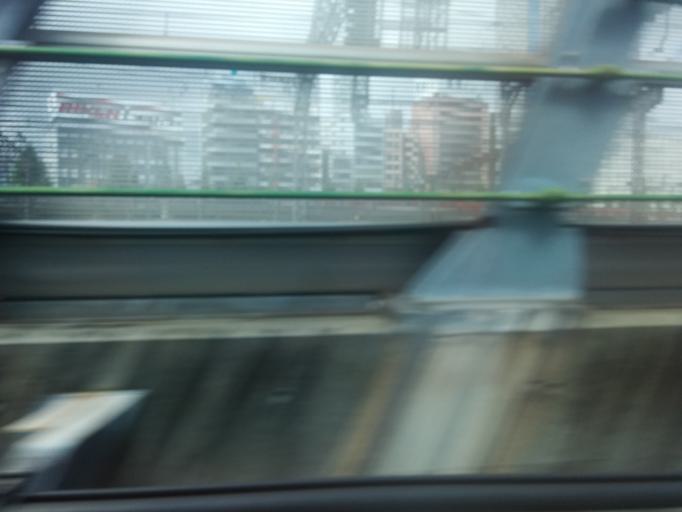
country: JP
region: Tokyo
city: Tokyo
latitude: 35.6256
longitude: 139.7392
